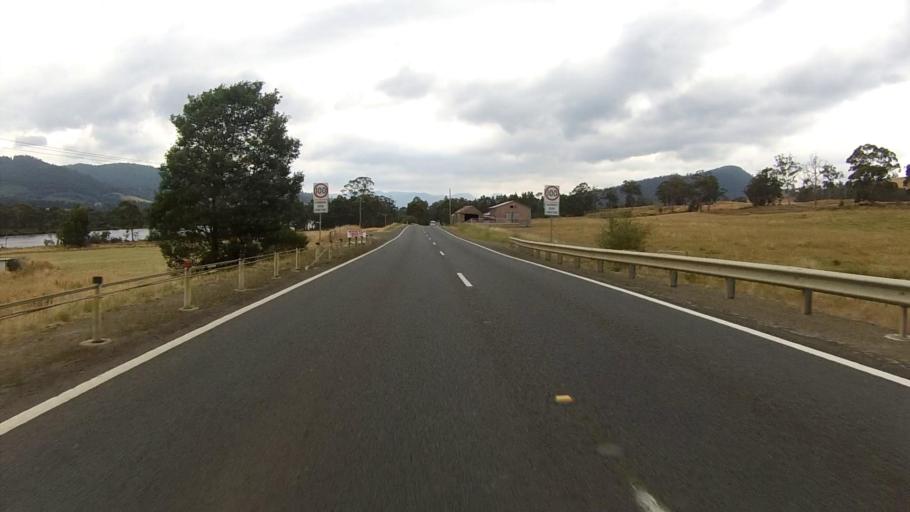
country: AU
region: Tasmania
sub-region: Huon Valley
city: Franklin
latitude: -43.0842
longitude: 147.0302
